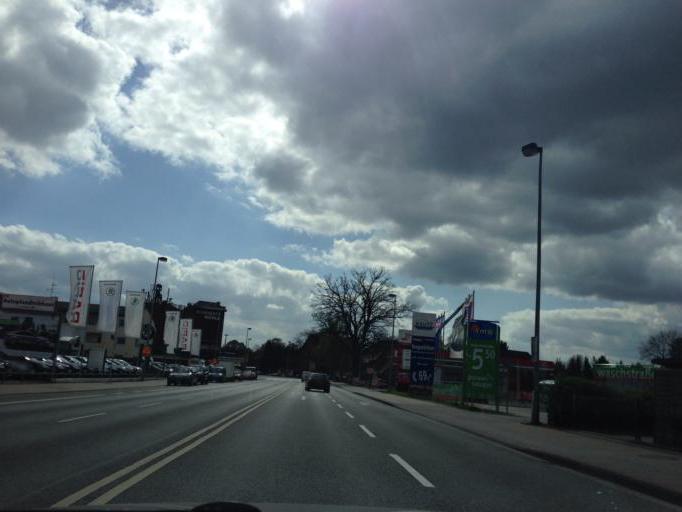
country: DE
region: Lower Saxony
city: Celle
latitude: 52.6039
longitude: 10.0724
